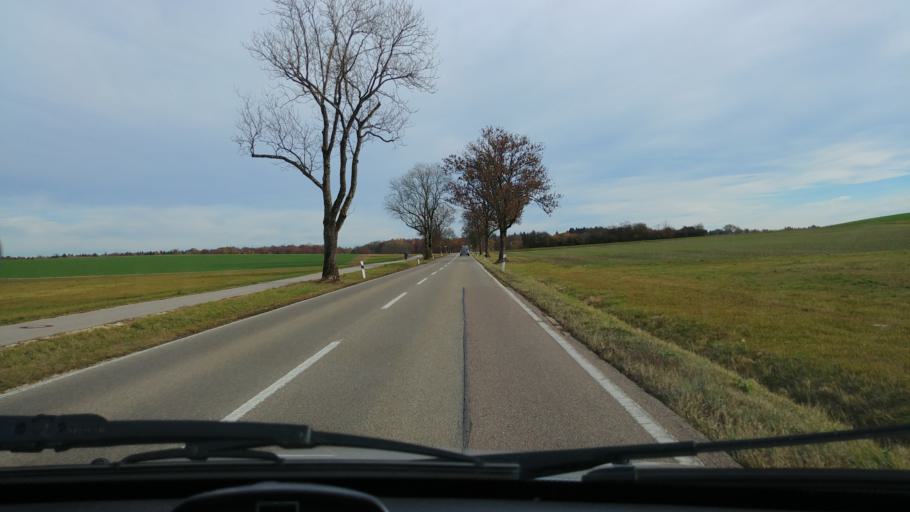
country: DE
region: Baden-Wuerttemberg
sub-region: Regierungsbezirk Stuttgart
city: Nattheim
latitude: 48.6606
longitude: 10.2097
